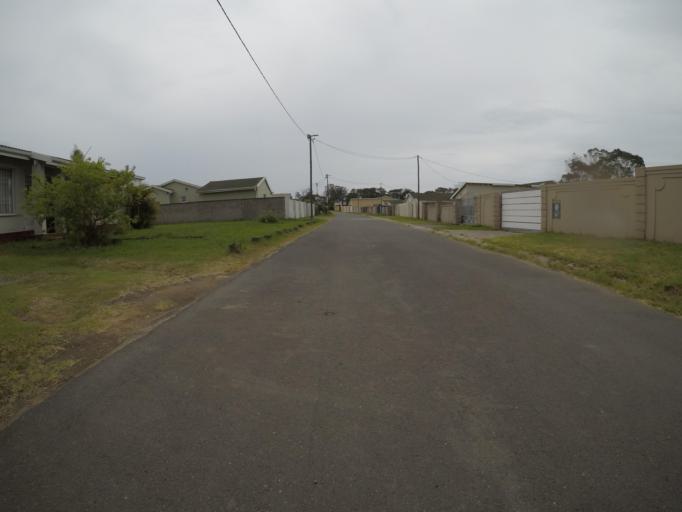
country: ZA
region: Eastern Cape
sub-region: Buffalo City Metropolitan Municipality
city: East London
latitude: -32.9990
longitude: 27.8468
